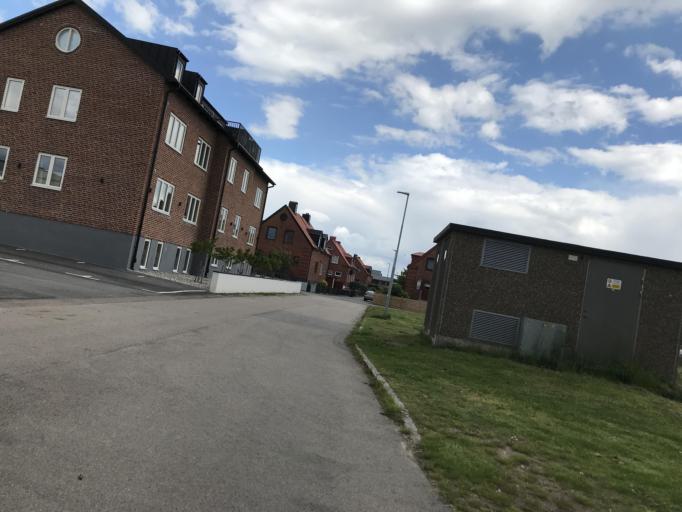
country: SE
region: Skane
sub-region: Landskrona
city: Landskrona
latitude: 55.8700
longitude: 12.8574
